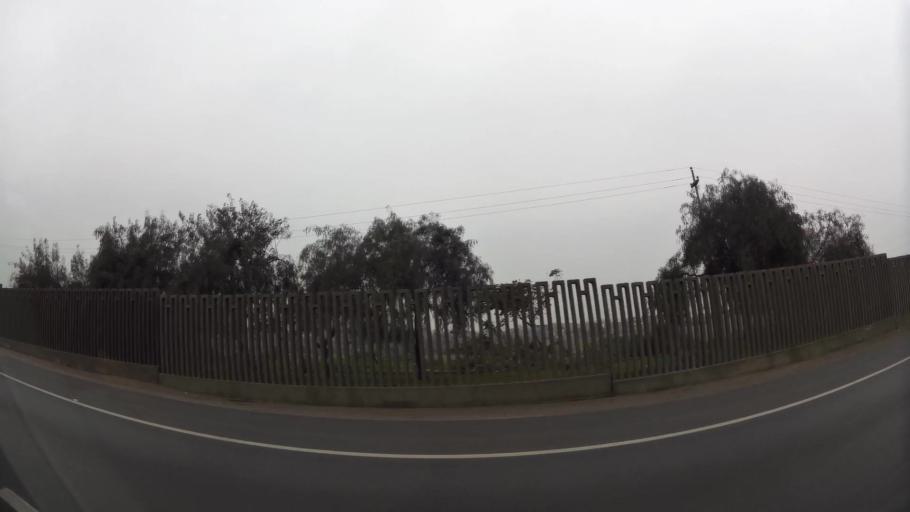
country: PE
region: Lima
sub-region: Lima
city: Vitarte
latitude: -12.0210
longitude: -76.9225
